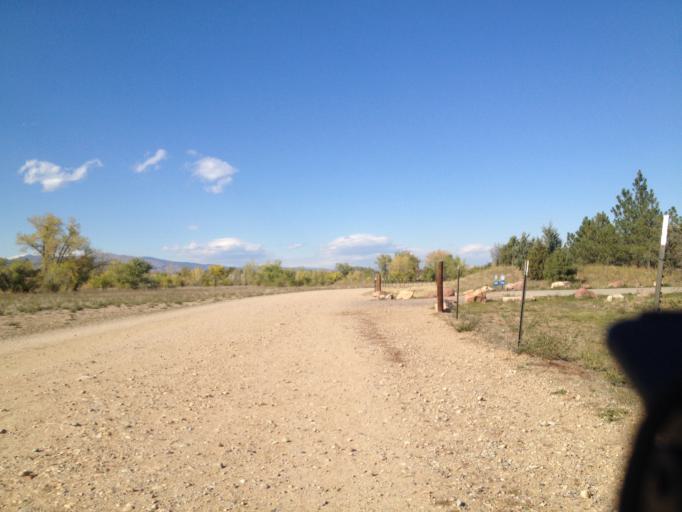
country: US
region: Colorado
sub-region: Boulder County
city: Boulder
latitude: 39.9798
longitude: -105.2334
